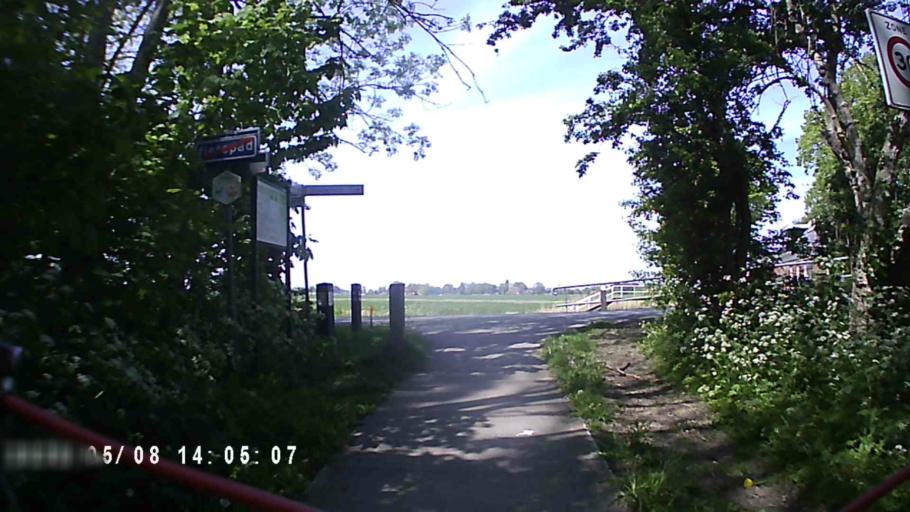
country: NL
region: Groningen
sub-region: Gemeente Appingedam
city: Appingedam
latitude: 53.3361
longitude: 6.8086
